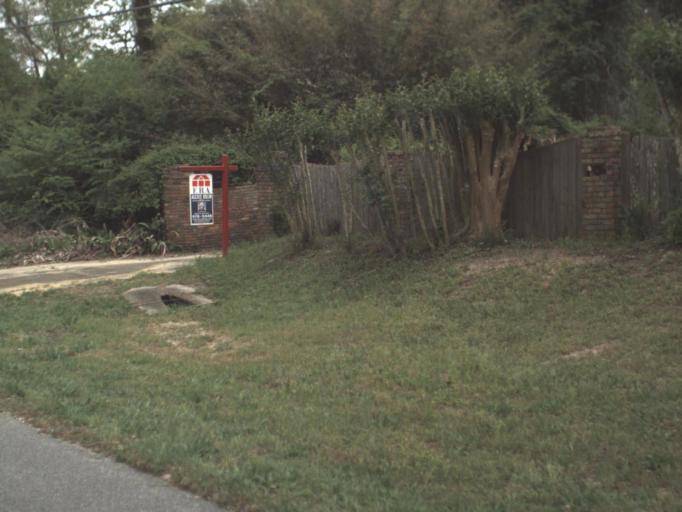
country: US
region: Florida
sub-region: Escambia County
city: Ferry Pass
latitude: 30.4930
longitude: -87.1566
